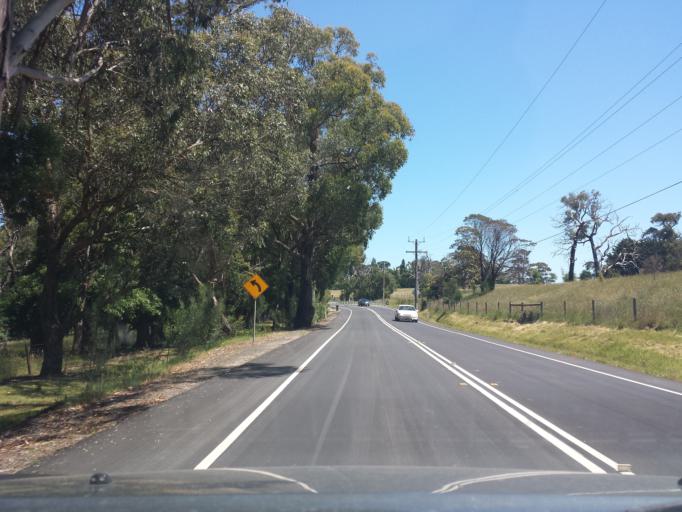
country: AU
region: Victoria
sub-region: Casey
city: Narre Warren North
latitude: -37.9909
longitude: 145.3511
